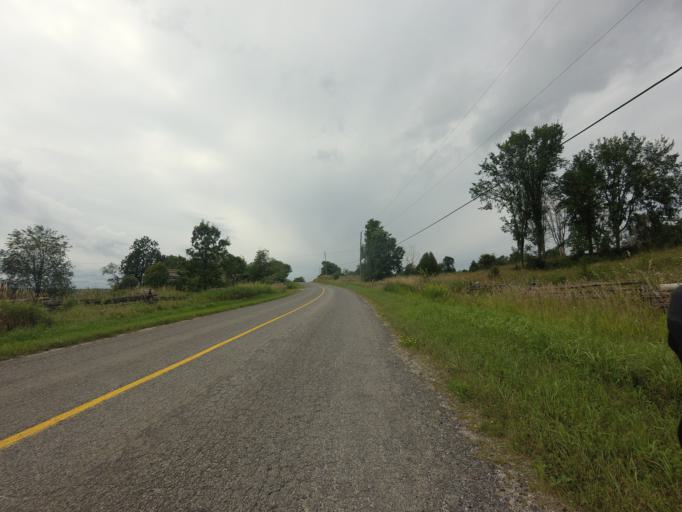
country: CA
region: Ontario
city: Perth
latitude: 44.8383
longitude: -76.5775
